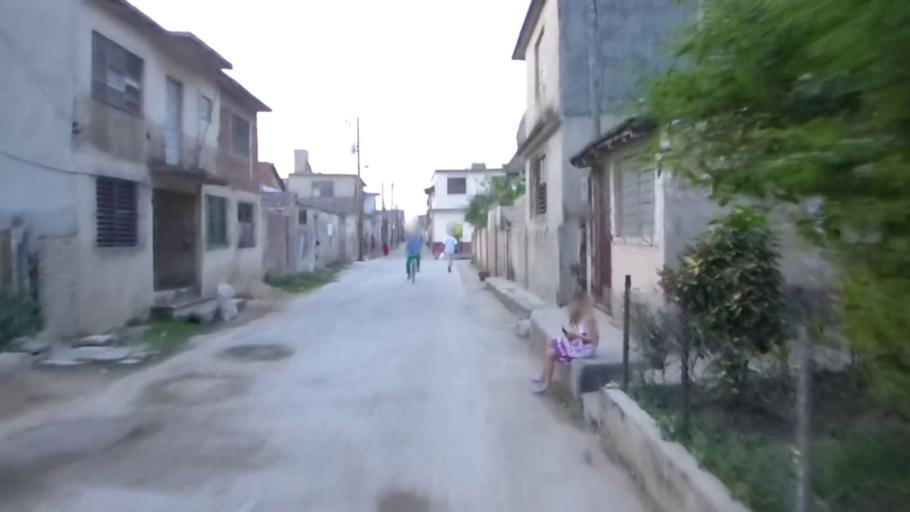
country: CU
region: Camaguey
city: Camaguey
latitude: 21.3735
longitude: -77.9193
